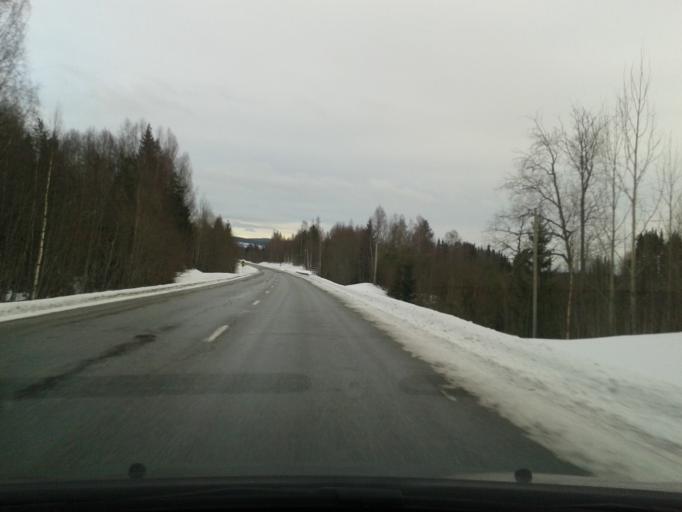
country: SE
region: Vaesternorrland
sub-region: Solleftea Kommun
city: As
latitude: 63.5840
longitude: 16.8224
